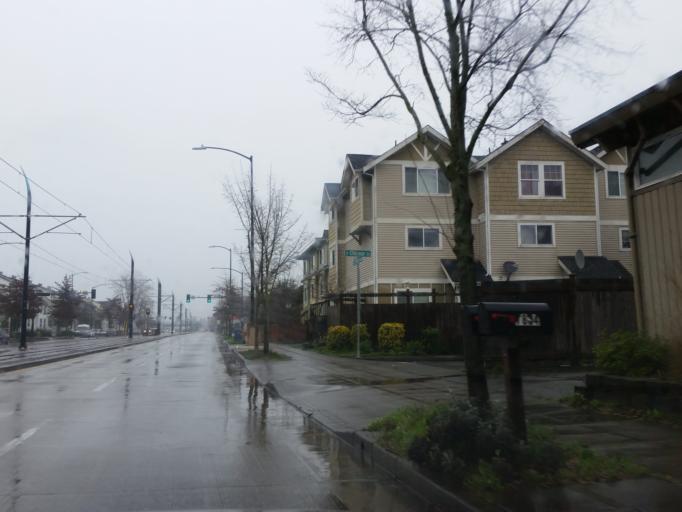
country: US
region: Washington
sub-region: King County
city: Riverton
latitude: 47.5323
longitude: -122.2806
